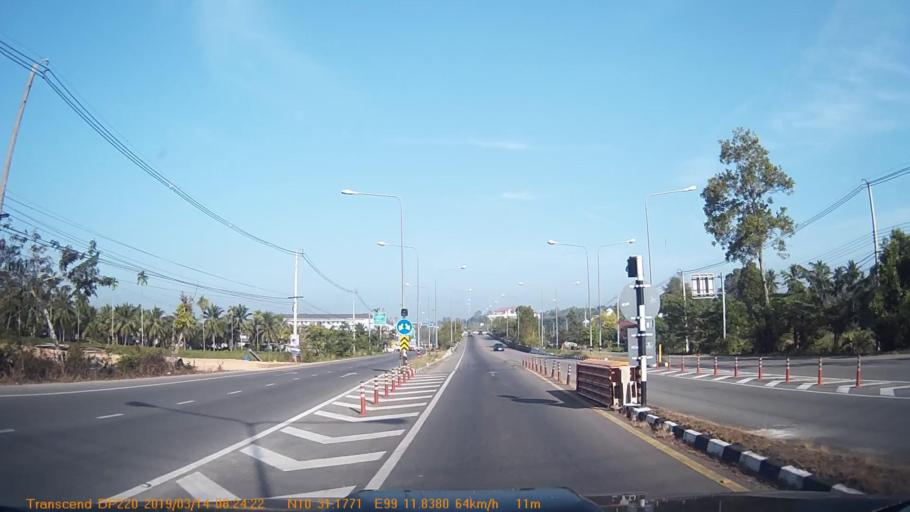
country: TH
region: Chumphon
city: Chumphon
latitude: 10.5197
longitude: 99.1972
